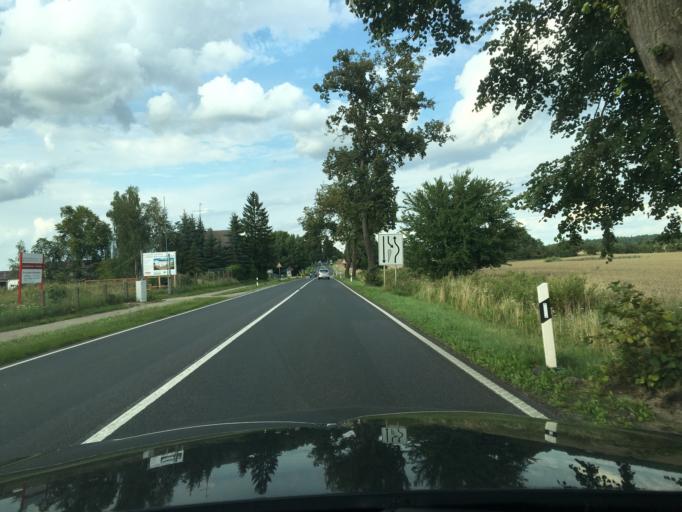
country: DE
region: Mecklenburg-Vorpommern
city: Neustrelitz
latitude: 53.4034
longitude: 13.1142
